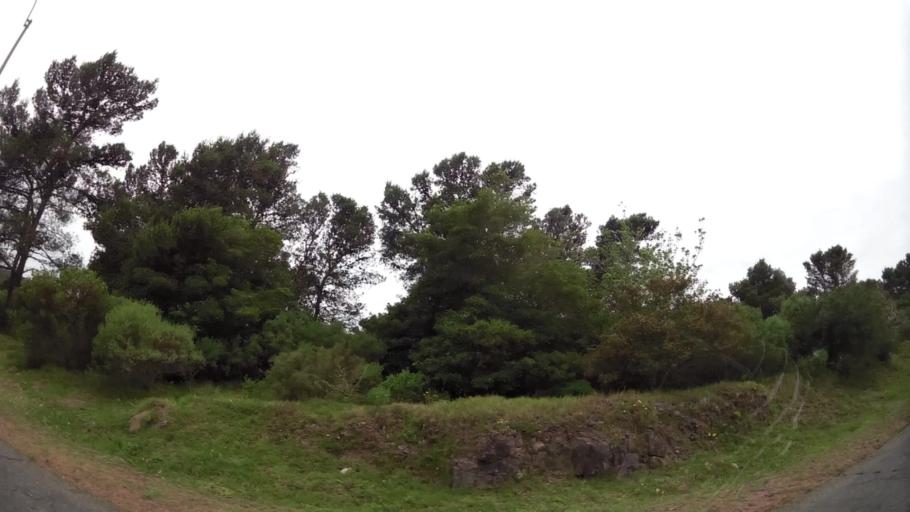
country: UY
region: Maldonado
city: Maldonado
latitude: -34.8978
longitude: -55.0385
